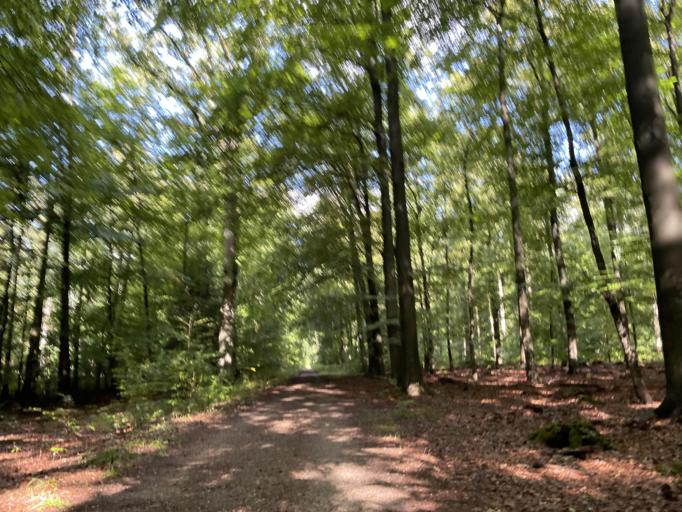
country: DE
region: Lower Saxony
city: Deutsch Evern
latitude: 53.2228
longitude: 10.4268
